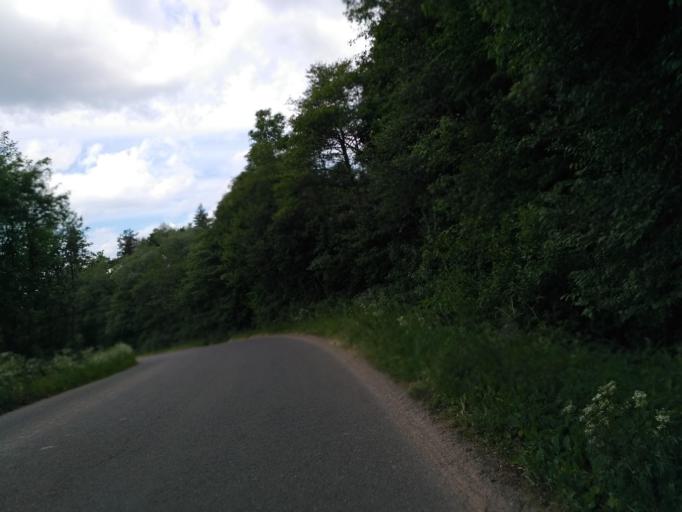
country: PL
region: Subcarpathian Voivodeship
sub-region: Powiat krosnienski
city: Chorkowka
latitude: 49.6229
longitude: 21.6512
